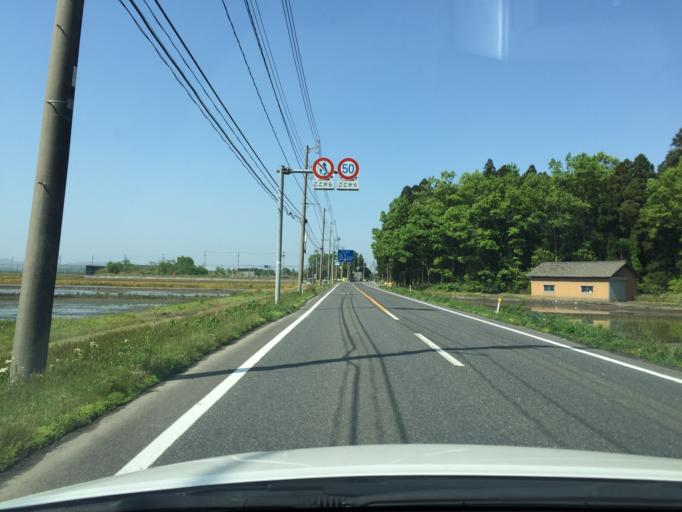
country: JP
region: Niigata
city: Gosen
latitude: 37.7200
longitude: 139.2252
